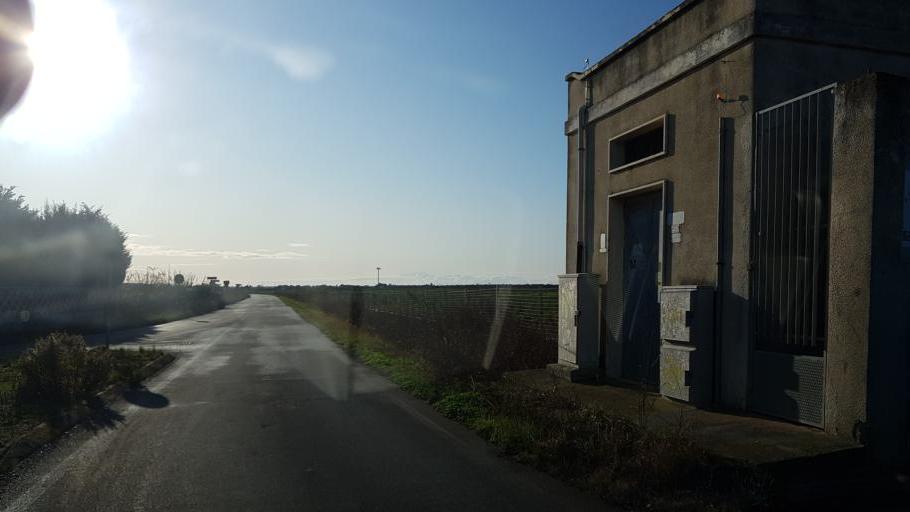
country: IT
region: Apulia
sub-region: Provincia di Brindisi
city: Torchiarolo
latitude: 40.5400
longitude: 18.0624
